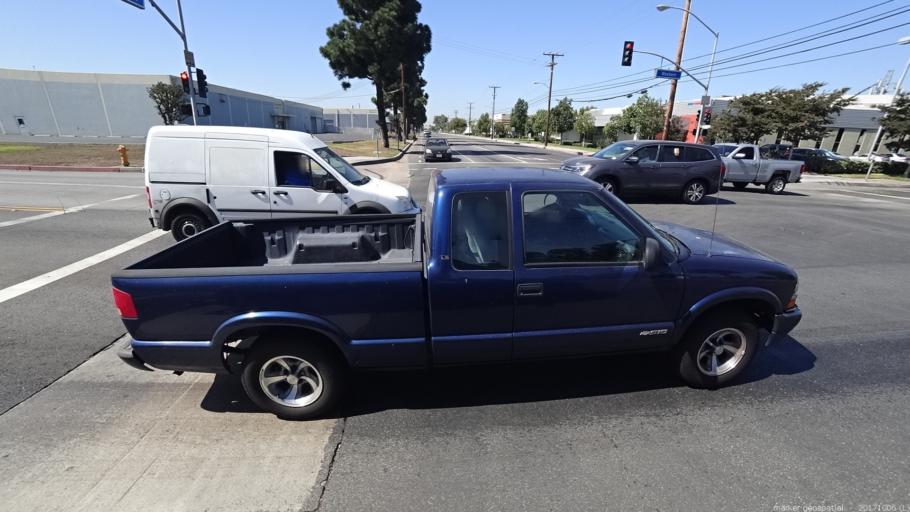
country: US
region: California
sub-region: Orange County
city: Westminster
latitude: 33.7810
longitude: -118.0014
